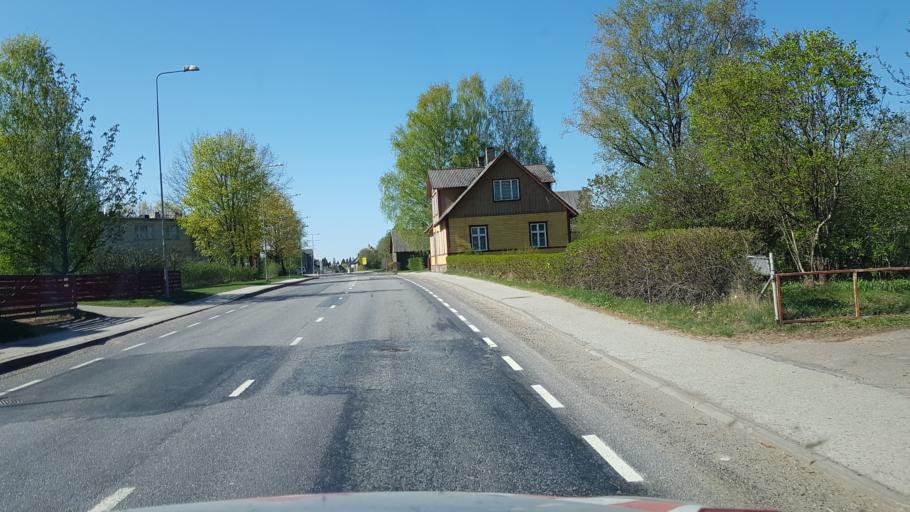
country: EE
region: Viljandimaa
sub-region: Karksi vald
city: Karksi-Nuia
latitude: 58.0994
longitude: 25.5590
